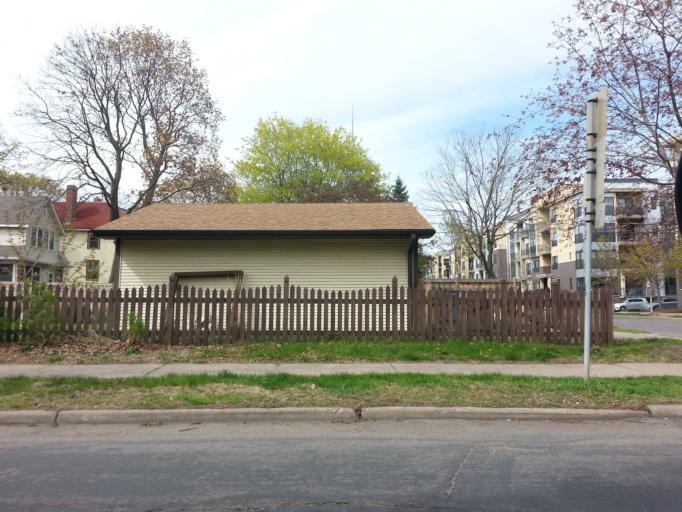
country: US
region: Minnesota
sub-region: Ramsey County
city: Lauderdale
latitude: 44.9647
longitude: -93.2080
